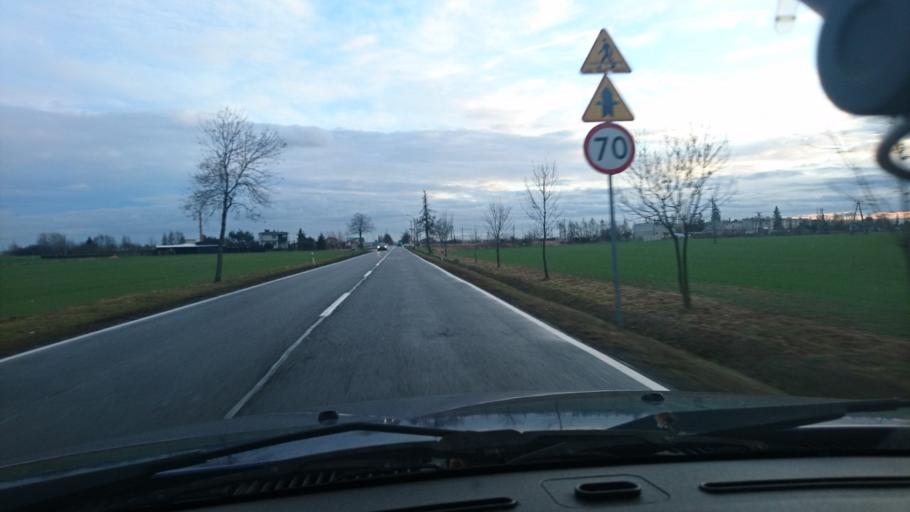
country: PL
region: Opole Voivodeship
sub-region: Powiat kluczborski
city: Kluczbork
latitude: 50.9981
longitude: 18.2072
